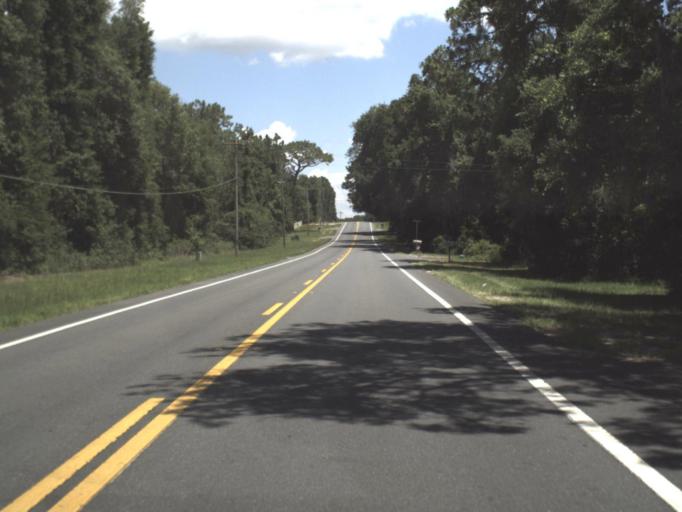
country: US
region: Florida
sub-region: Alachua County
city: Hawthorne
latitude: 29.6486
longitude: -82.0330
